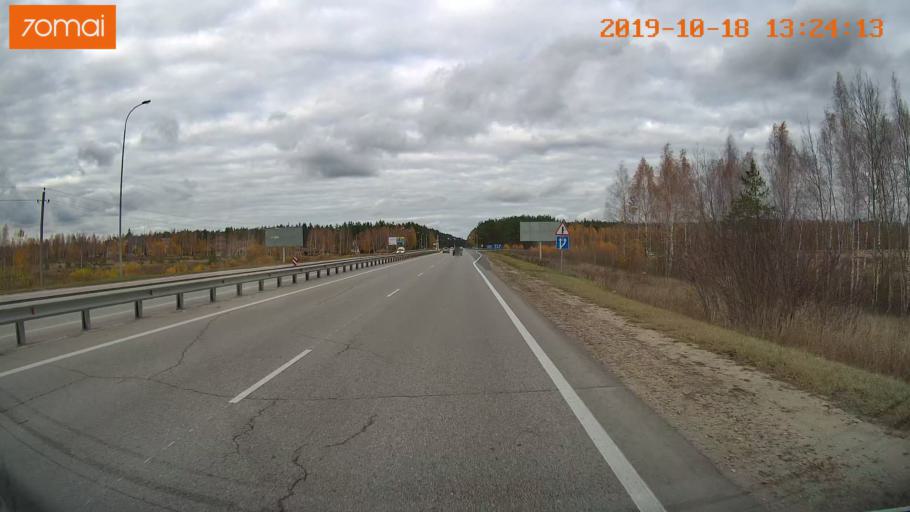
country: RU
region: Rjazan
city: Polyany
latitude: 54.7276
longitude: 39.8453
